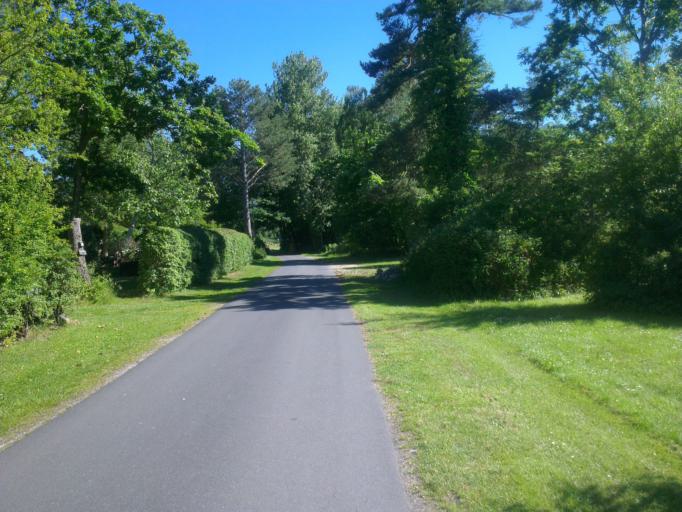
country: DK
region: Capital Region
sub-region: Halsnaes Kommune
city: Hundested
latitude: 55.9193
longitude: 11.9033
